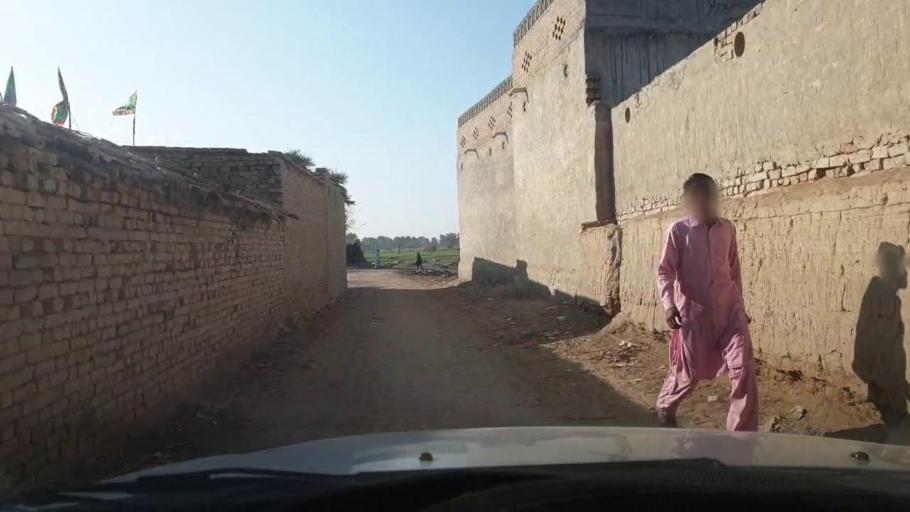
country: PK
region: Sindh
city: Mirpur Mathelo
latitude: 28.0355
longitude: 69.5924
